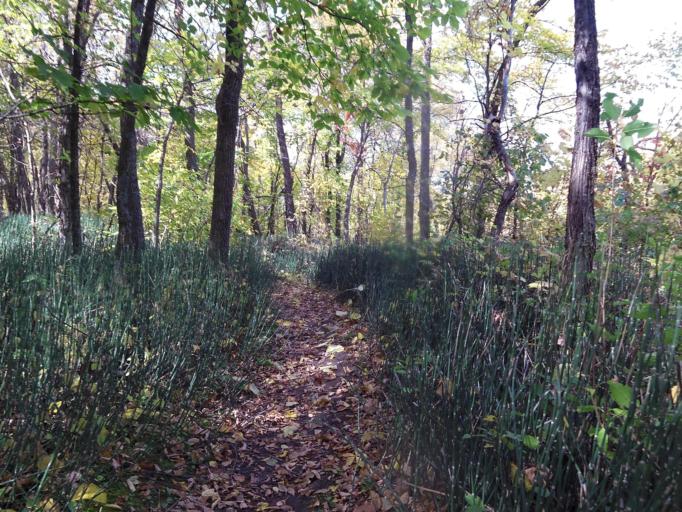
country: US
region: North Dakota
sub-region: Pembina County
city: Cavalier
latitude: 48.7760
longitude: -97.7389
